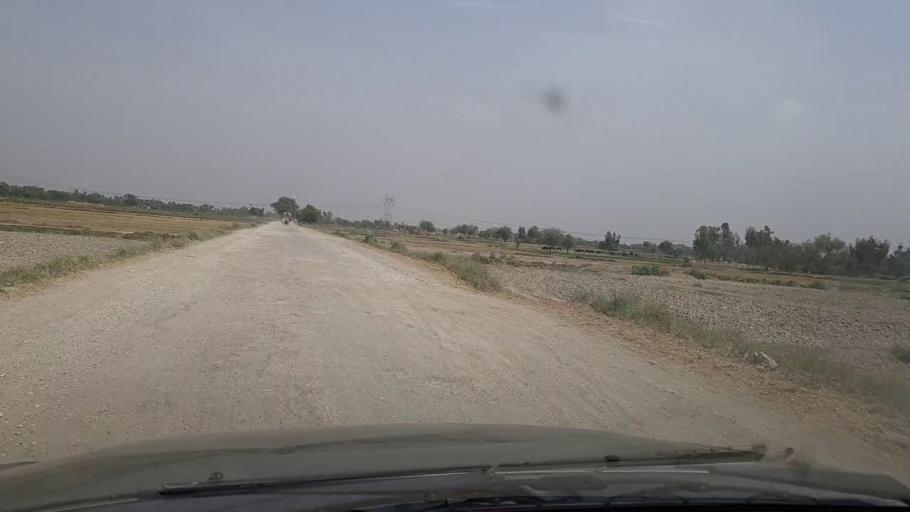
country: PK
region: Sindh
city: Shikarpur
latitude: 27.9227
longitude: 68.6731
